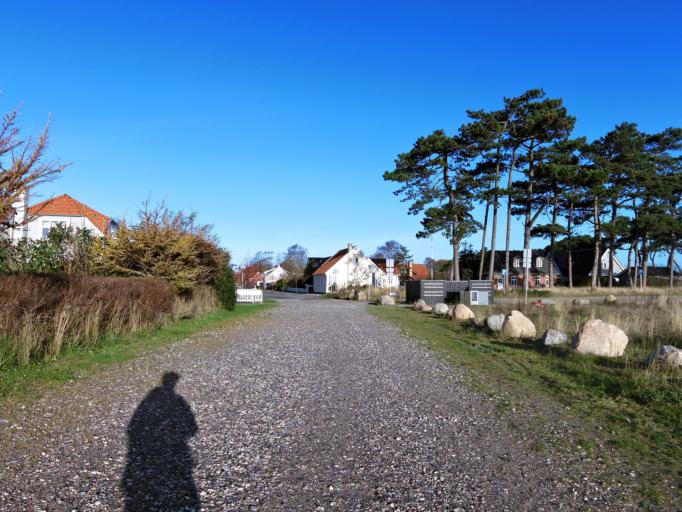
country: DK
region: Central Jutland
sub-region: Odder Kommune
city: Odder
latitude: 55.9131
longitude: 10.2558
